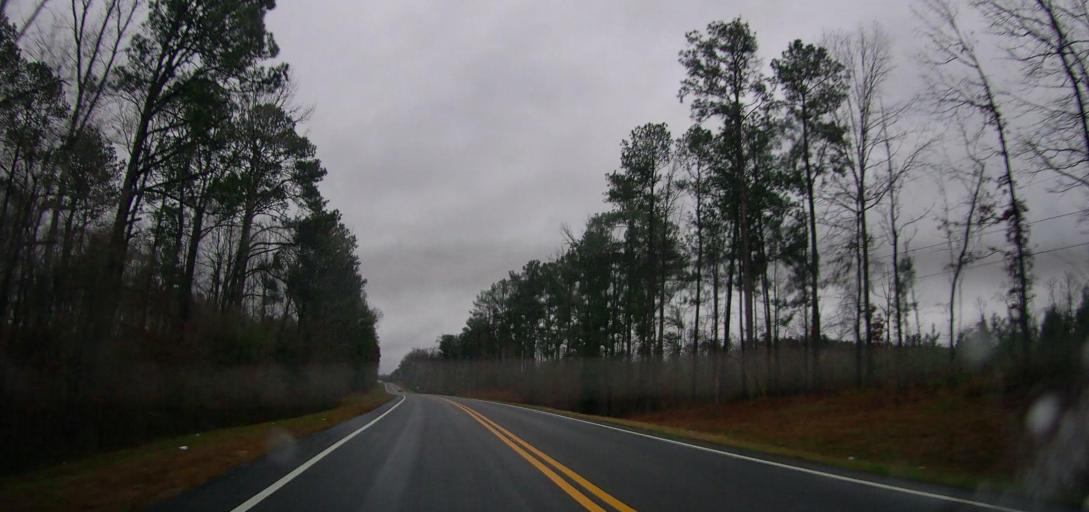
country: US
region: Alabama
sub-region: Bibb County
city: Centreville
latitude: 32.8318
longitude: -86.9525
